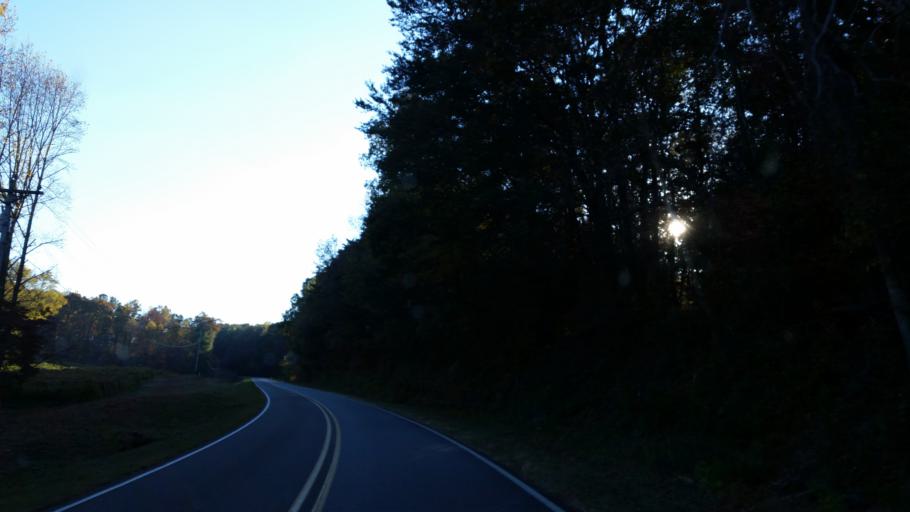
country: US
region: Georgia
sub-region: Gilmer County
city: Ellijay
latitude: 34.6144
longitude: -84.3932
